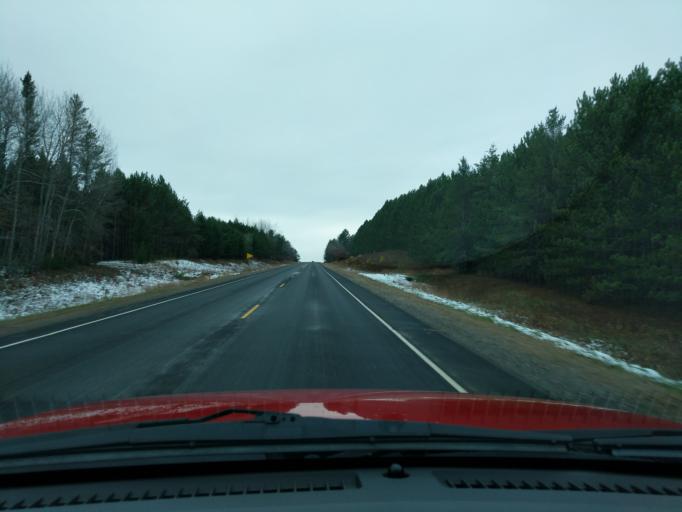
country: US
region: Wisconsin
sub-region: Sawyer County
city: Hayward
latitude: 45.8221
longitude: -91.5711
